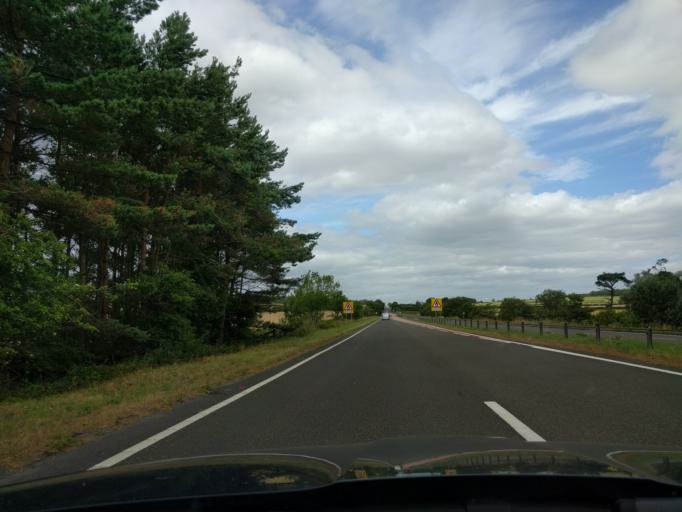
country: GB
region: England
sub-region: Northumberland
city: Alnwick
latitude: 55.4288
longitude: -1.6888
